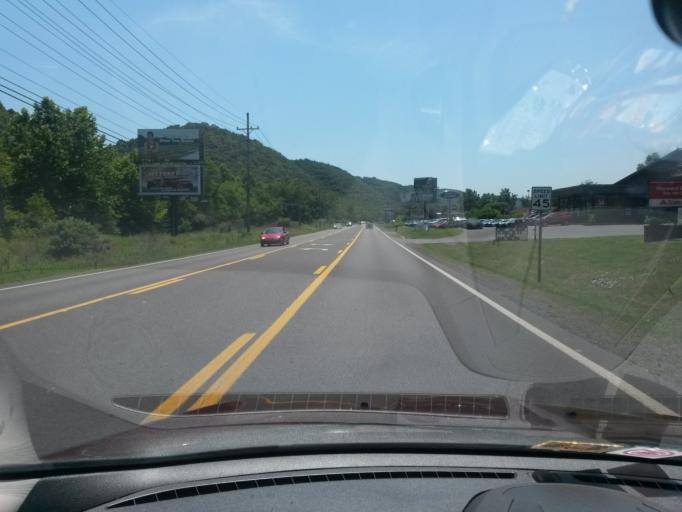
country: US
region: West Virginia
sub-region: Mineral County
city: Keyser
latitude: 39.4159
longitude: -78.9995
